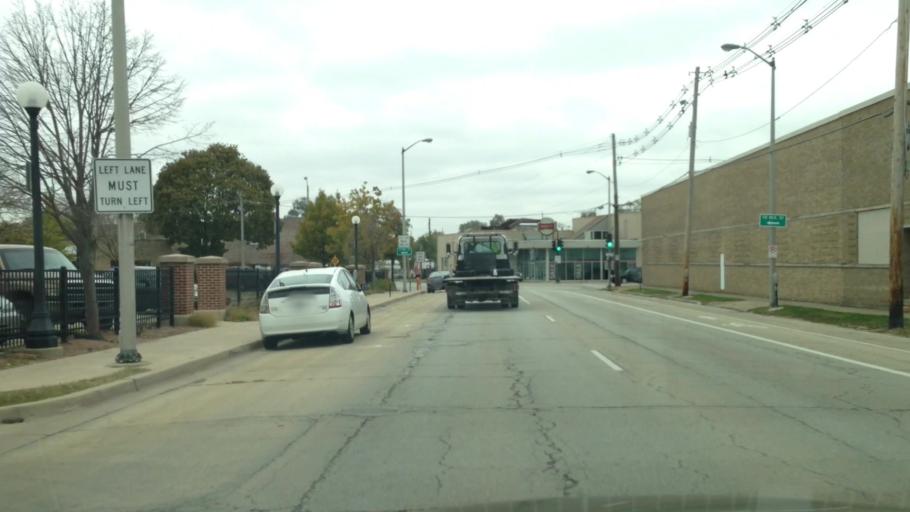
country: US
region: Illinois
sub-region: Champaign County
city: Champaign
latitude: 40.1192
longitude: -88.2415
